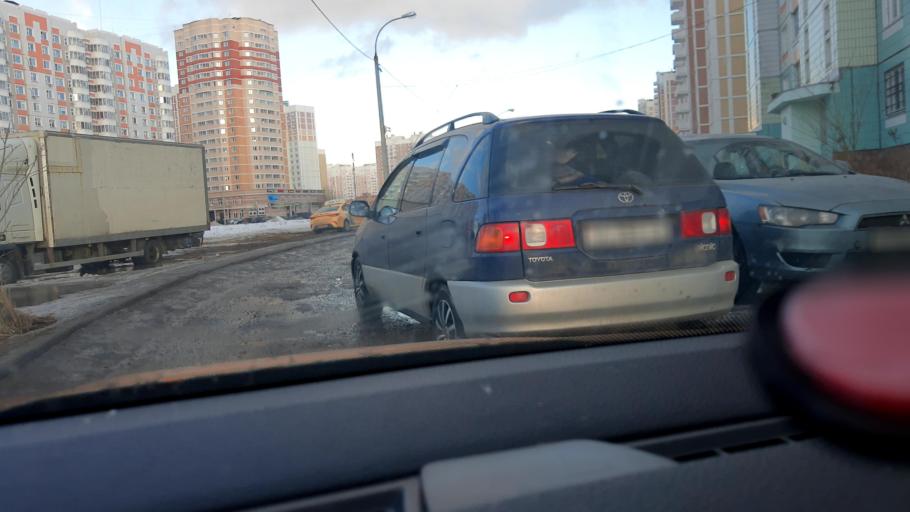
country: RU
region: Moskovskaya
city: Dubrovitsy
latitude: 55.4193
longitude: 37.4765
